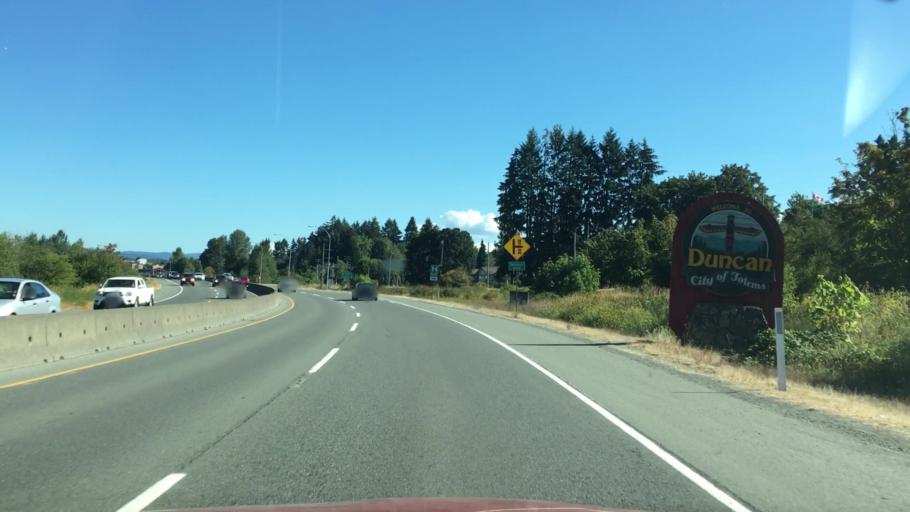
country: CA
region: British Columbia
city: Duncan
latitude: 48.7938
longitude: -123.7138
